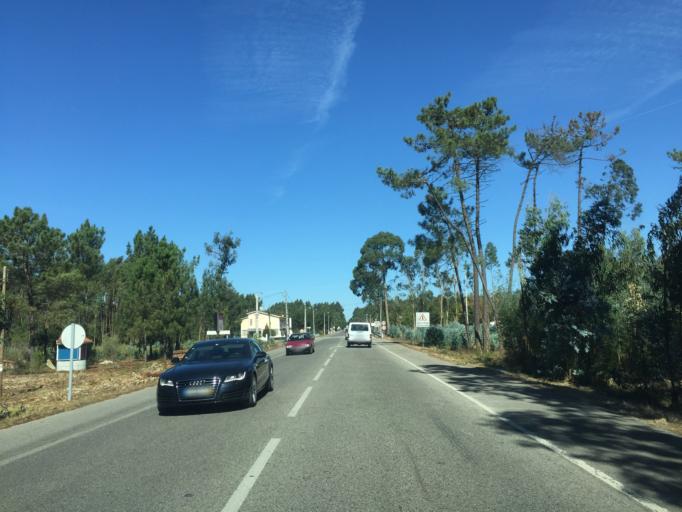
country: PT
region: Coimbra
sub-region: Figueira da Foz
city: Alhadas
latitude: 40.2893
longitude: -8.7667
